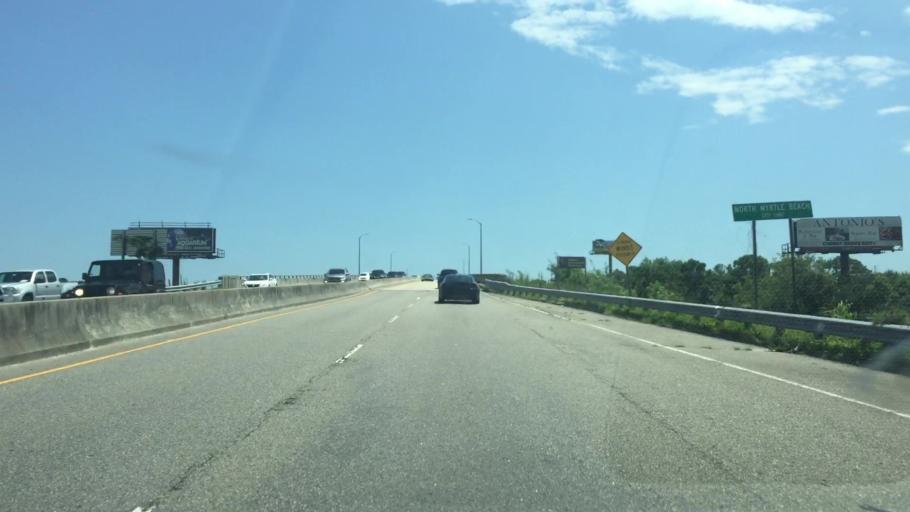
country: US
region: South Carolina
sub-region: Horry County
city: Little River
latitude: 33.8560
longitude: -78.6554
